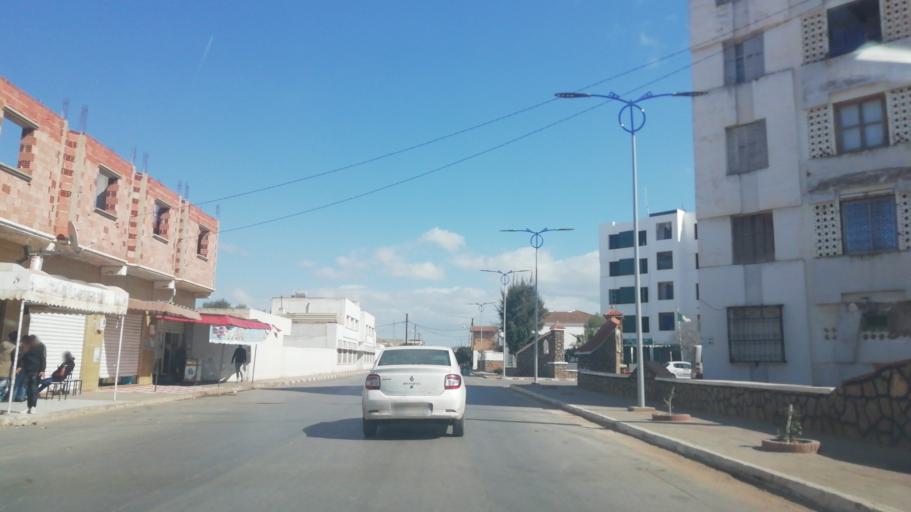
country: DZ
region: Mostaganem
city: Mostaganem
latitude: 35.9999
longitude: 0.3347
